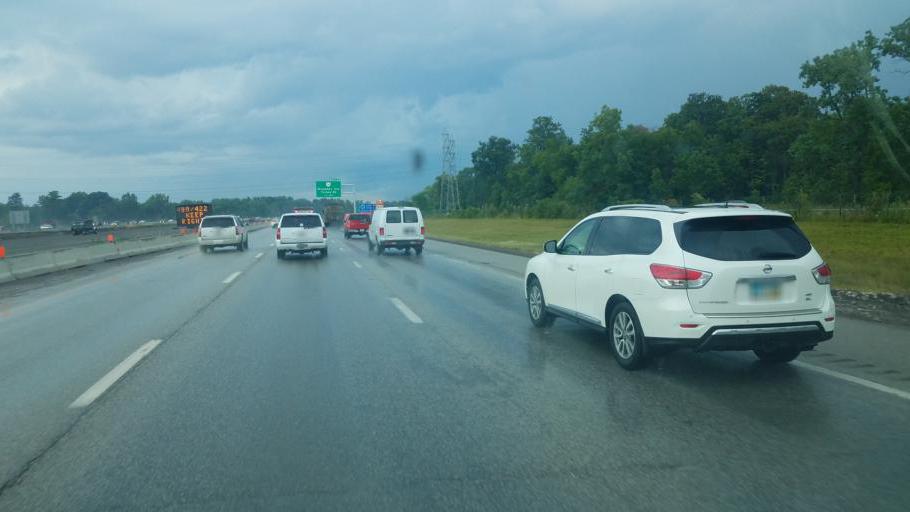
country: US
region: Ohio
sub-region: Cuyahoga County
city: Oakwood
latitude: 41.3605
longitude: -81.5146
